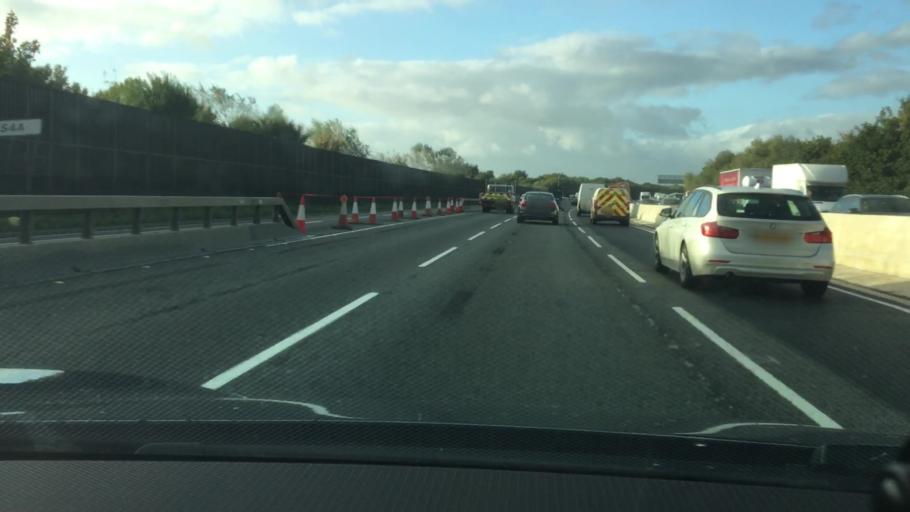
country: GB
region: England
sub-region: Derbyshire
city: Long Eaton
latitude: 52.8956
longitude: -1.2991
